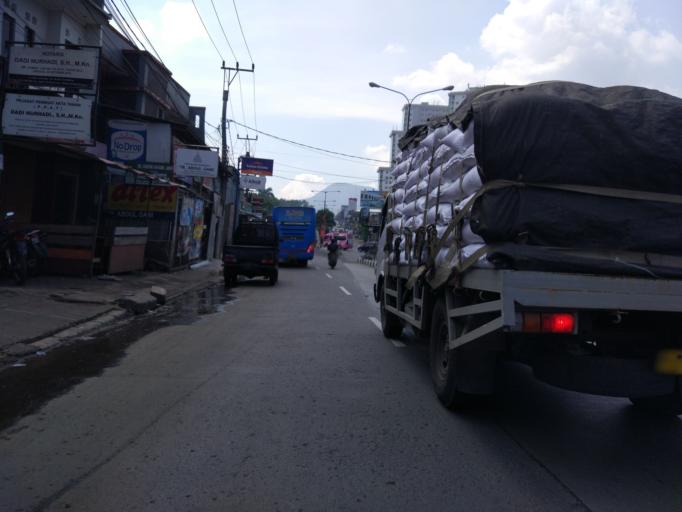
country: ID
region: West Java
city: Cileunyi
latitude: -6.9365
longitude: 107.7621
